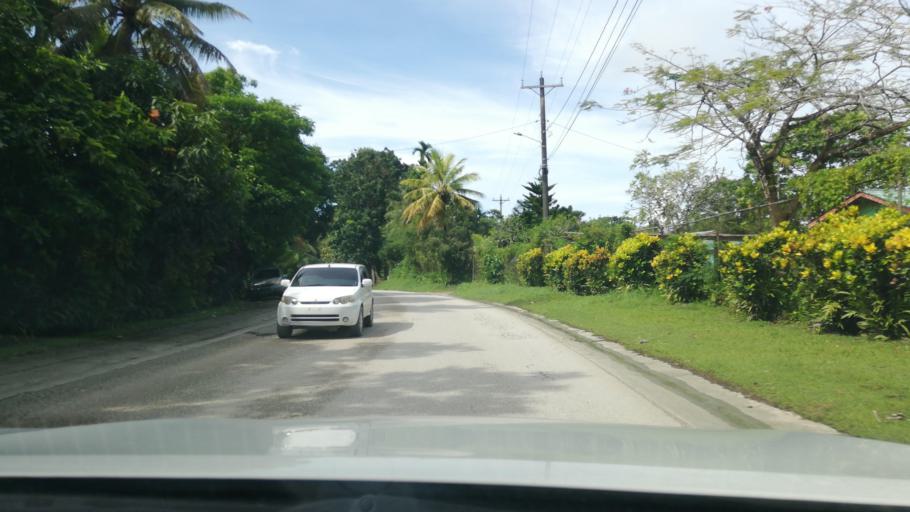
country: FM
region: Yap
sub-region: Weloy Municipality
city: Colonia
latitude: 9.5155
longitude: 138.1108
